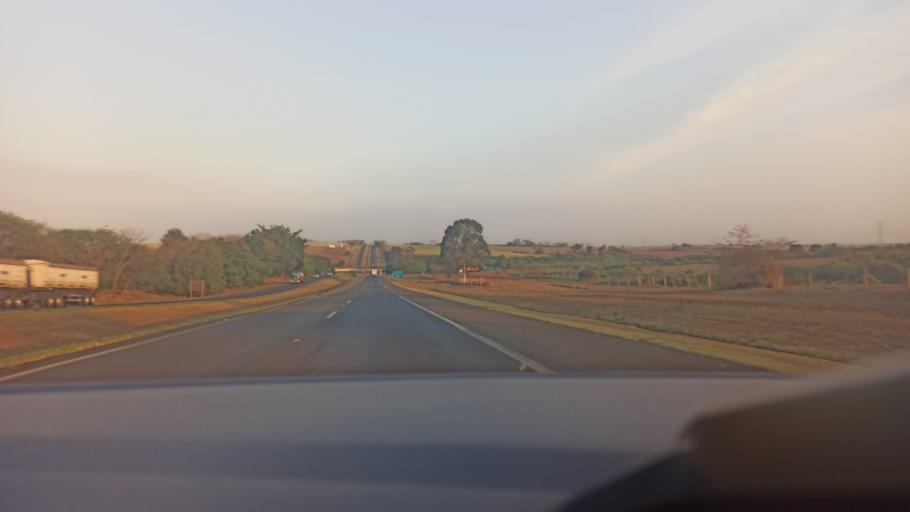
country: BR
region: Sao Paulo
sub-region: Santa Adelia
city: Santa Adelia
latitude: -21.3680
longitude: -48.7539
